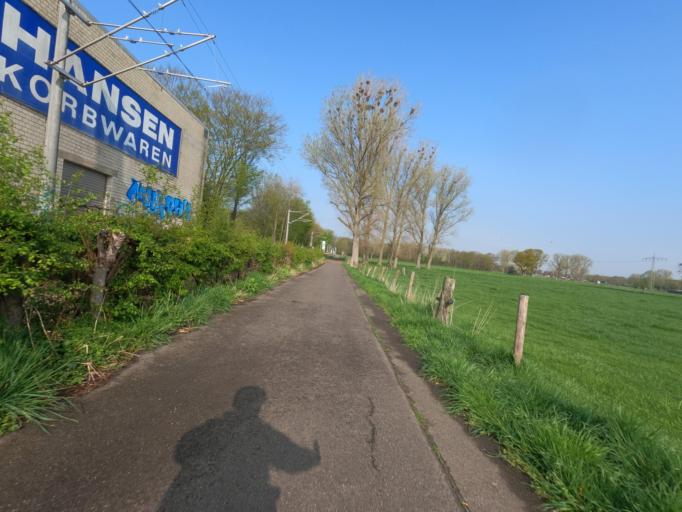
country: DE
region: North Rhine-Westphalia
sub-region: Regierungsbezirk Koln
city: Heinsberg
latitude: 51.0466
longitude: 6.1497
